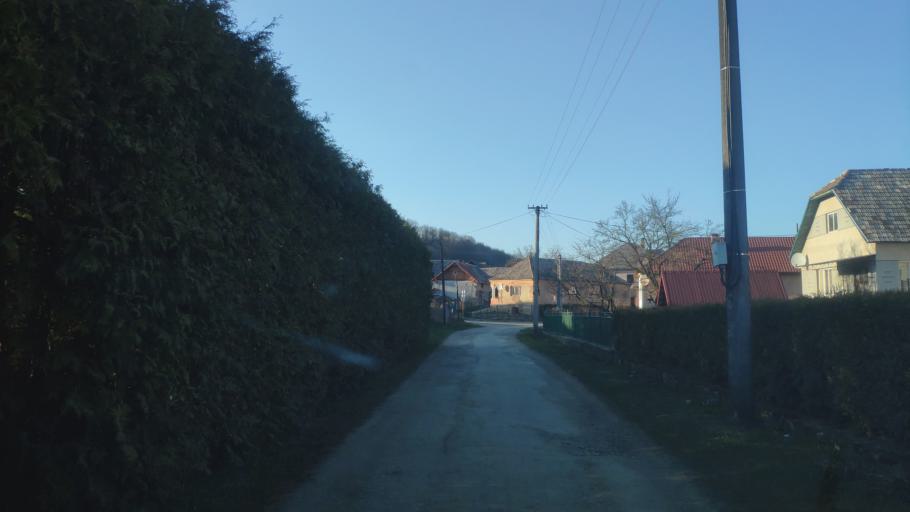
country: HU
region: Borsod-Abauj-Zemplen
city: Putnok
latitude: 48.5141
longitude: 20.3298
